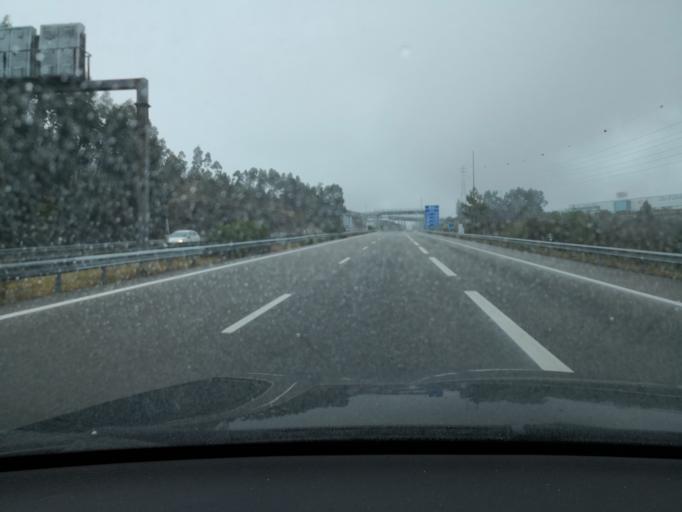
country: PT
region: Porto
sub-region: Pacos de Ferreira
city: Seroa
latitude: 41.2424
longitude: -8.4354
